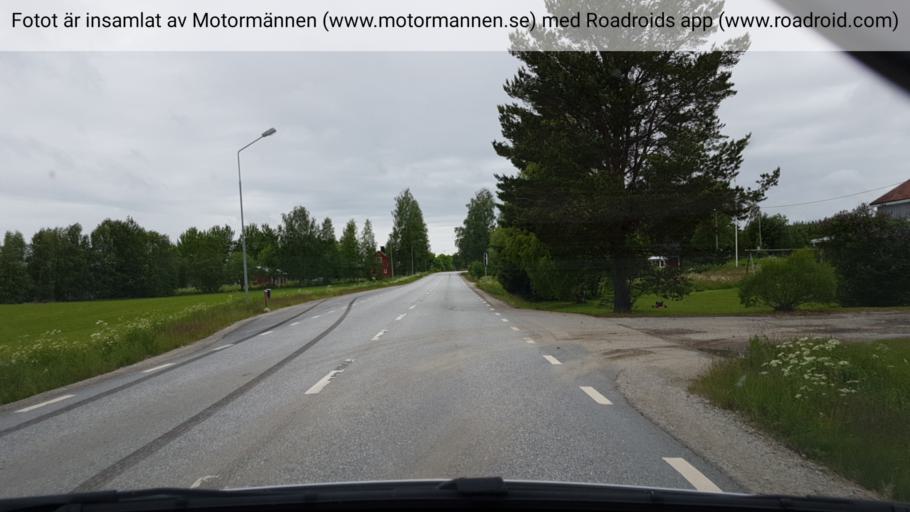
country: SE
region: Vaesterbotten
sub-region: Vindelns Kommun
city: Vindeln
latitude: 64.1604
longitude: 19.5020
